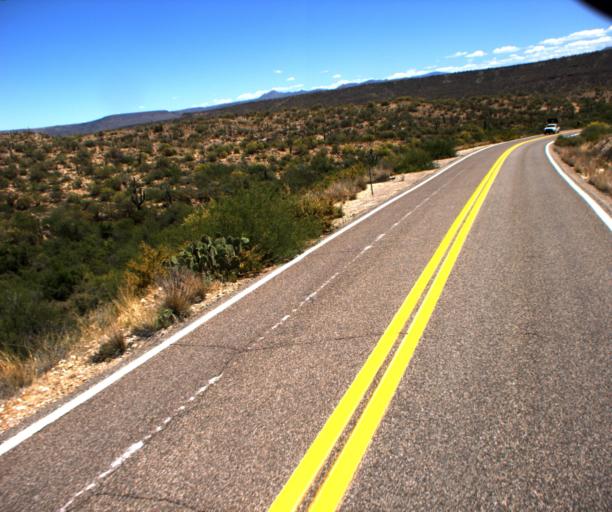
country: US
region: Arizona
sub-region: Yavapai County
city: Bagdad
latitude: 34.5186
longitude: -113.0945
